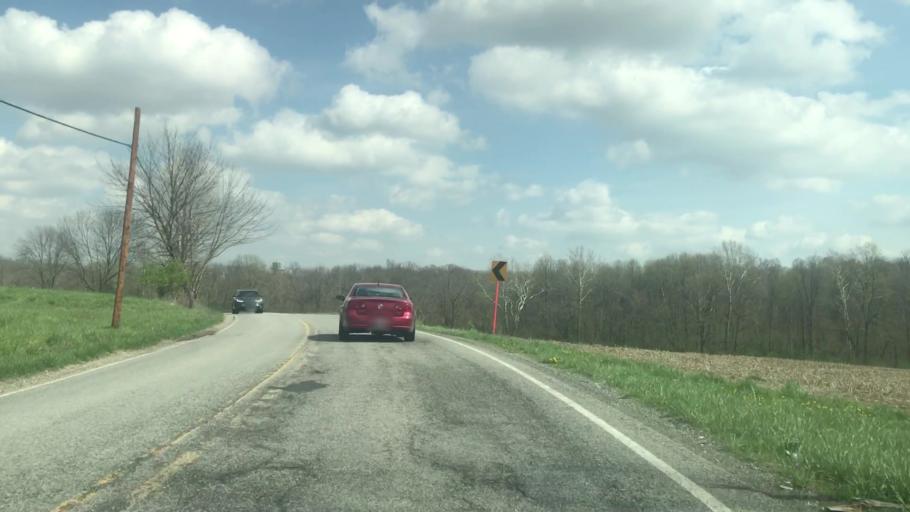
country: US
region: Indiana
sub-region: Johnson County
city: Waterloo
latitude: 39.5529
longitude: -86.2162
